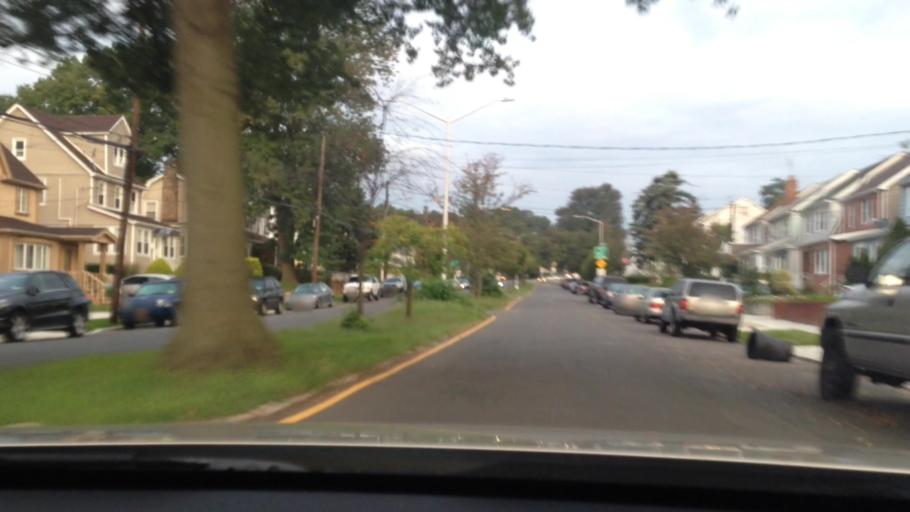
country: US
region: New York
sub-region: Nassau County
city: Bellerose Terrace
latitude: 40.7223
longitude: -73.7527
